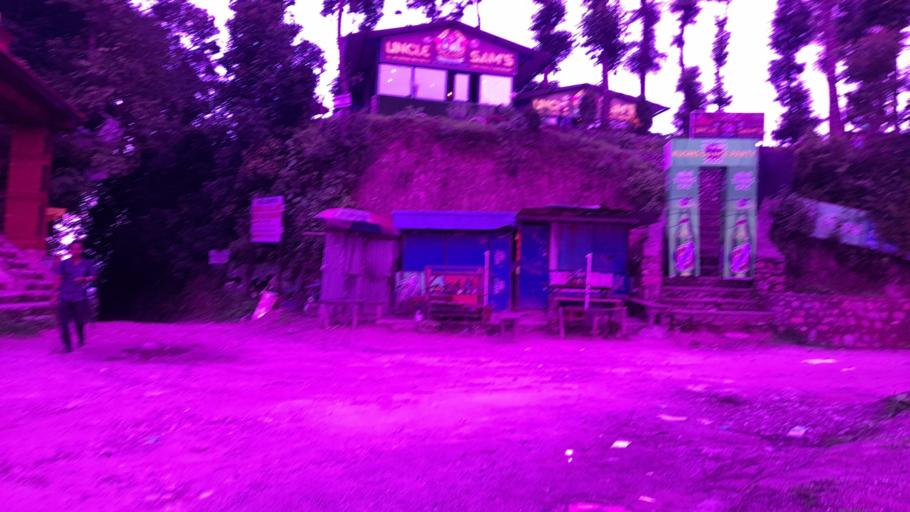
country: NP
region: Central Region
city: Banepa
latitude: 27.6102
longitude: 85.5676
